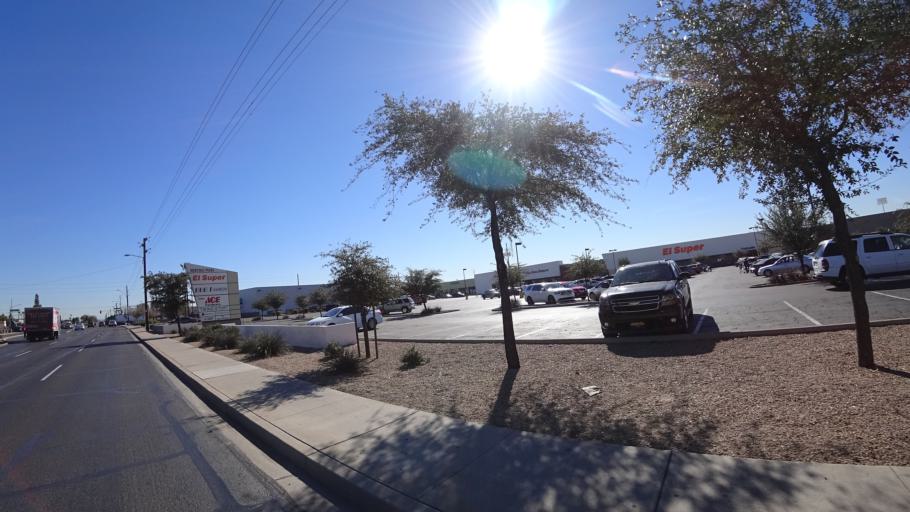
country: US
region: Arizona
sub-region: Maricopa County
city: Glendale
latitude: 33.4949
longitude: -112.1709
